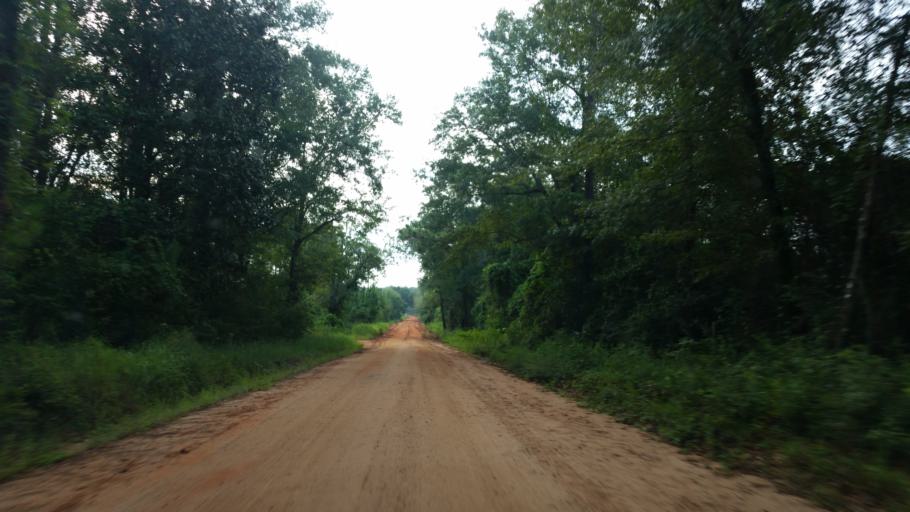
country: US
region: Alabama
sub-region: Escambia County
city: Atmore
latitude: 30.7931
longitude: -87.5415
